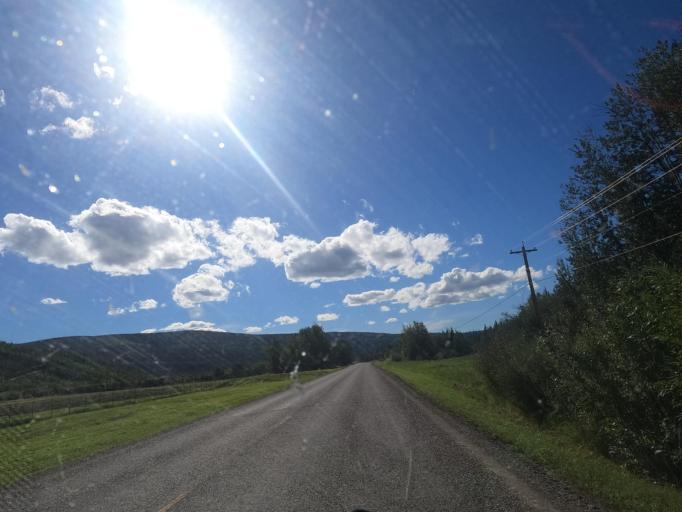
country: CA
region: Yukon
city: Dawson City
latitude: 64.0377
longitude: -139.1475
